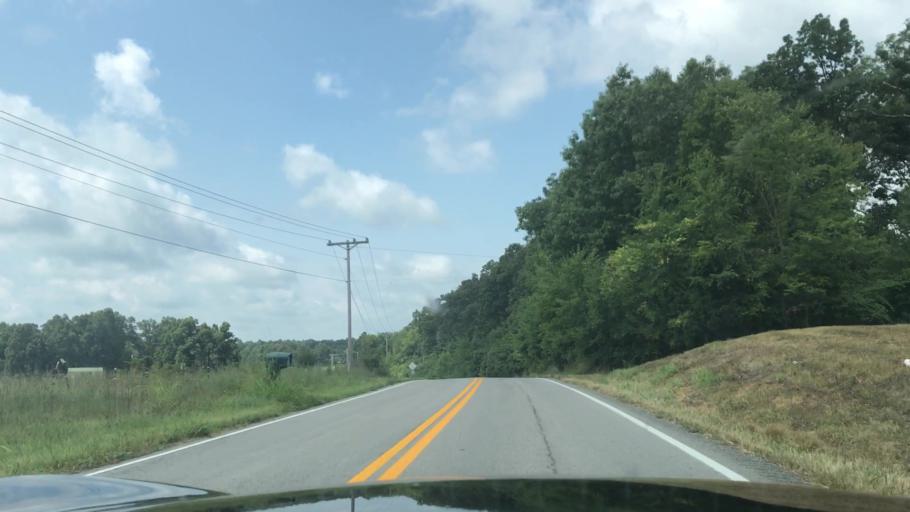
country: US
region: Kentucky
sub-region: Ohio County
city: Beaver Dam
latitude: 37.2092
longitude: -86.9318
